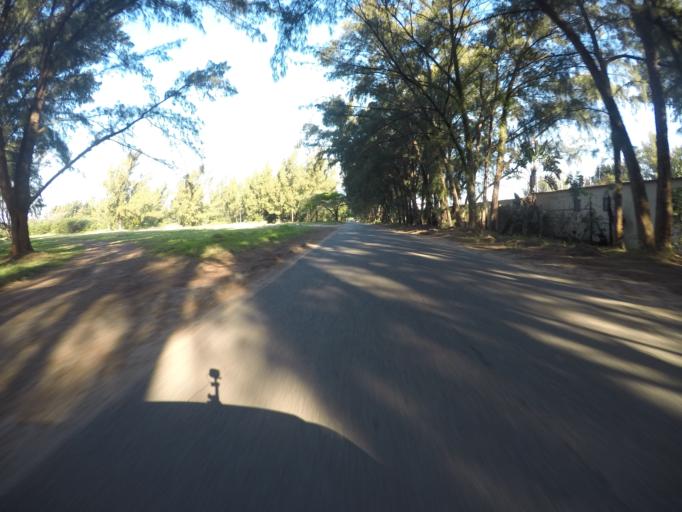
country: ZA
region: KwaZulu-Natal
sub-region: uThungulu District Municipality
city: Richards Bay
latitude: -28.7901
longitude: 32.0840
